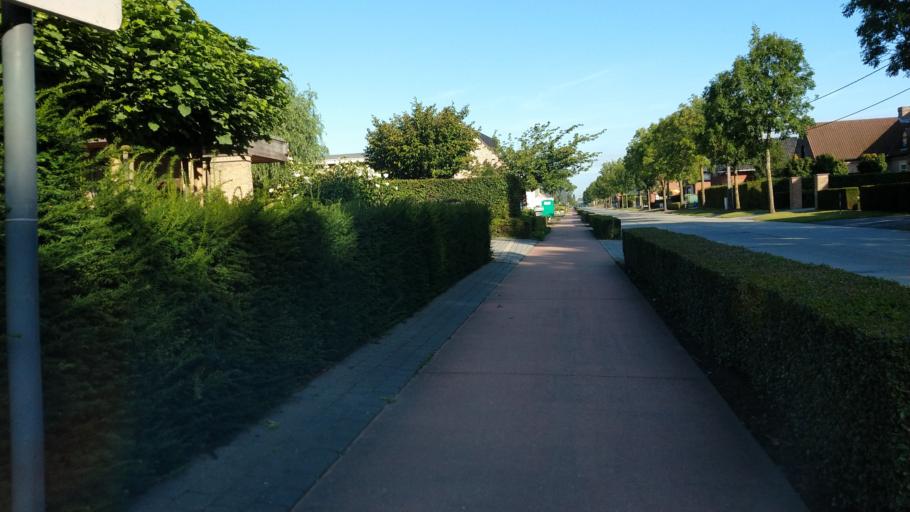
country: BE
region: Flanders
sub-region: Provincie Oost-Vlaanderen
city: Lochristi
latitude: 51.1011
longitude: 3.8430
